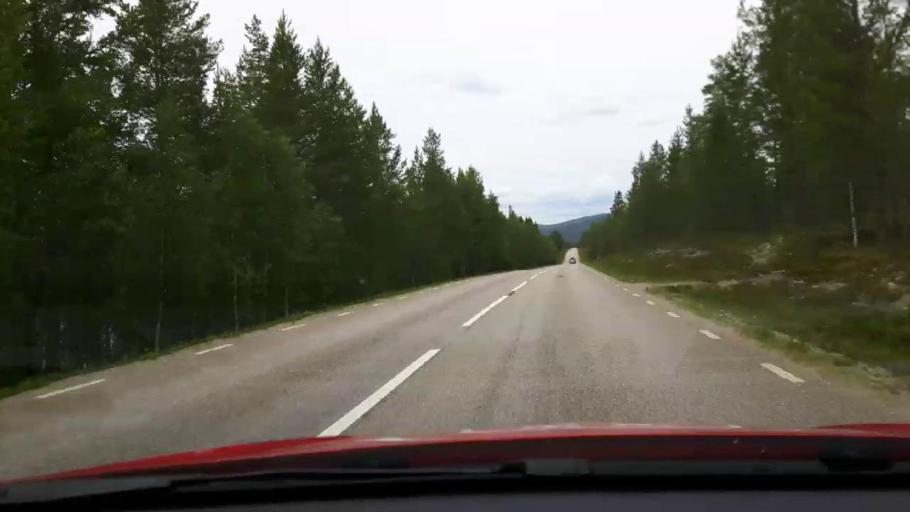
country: SE
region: Jaemtland
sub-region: Harjedalens Kommun
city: Sveg
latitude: 62.2468
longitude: 13.8434
